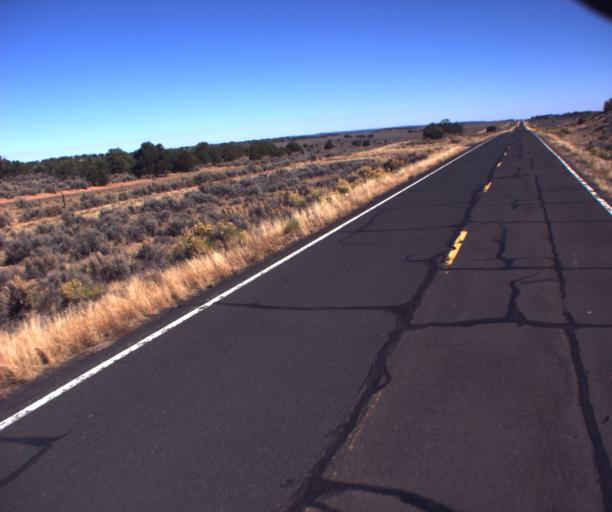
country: US
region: Arizona
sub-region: Navajo County
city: First Mesa
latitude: 35.7409
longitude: -110.0736
